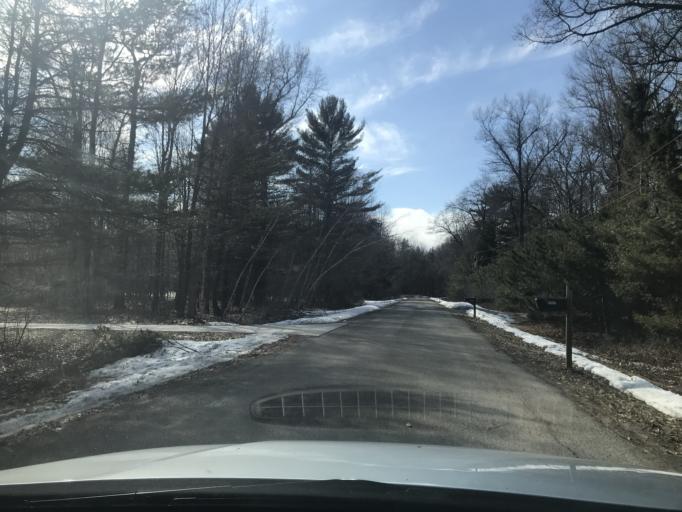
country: US
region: Wisconsin
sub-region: Marinette County
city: Marinette
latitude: 45.0430
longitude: -87.6690
